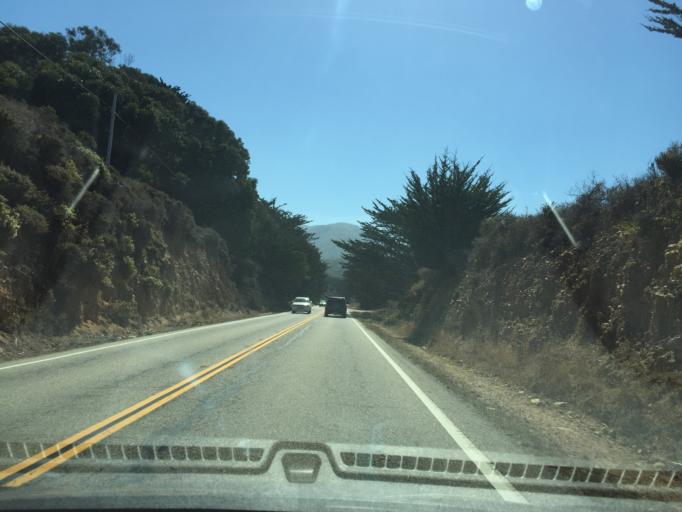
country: US
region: California
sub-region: Monterey County
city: Carmel-by-the-Sea
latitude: 36.3870
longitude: -121.9008
